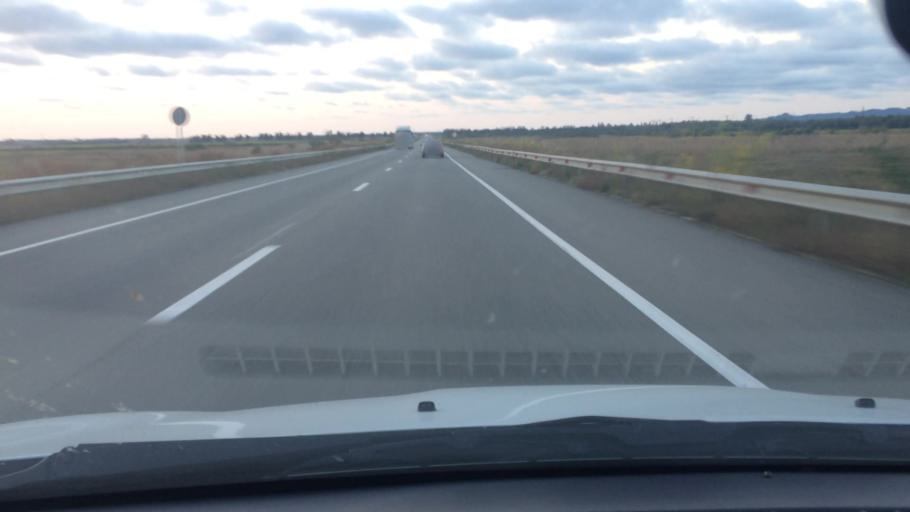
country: GE
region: Ajaria
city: Ochkhamuri
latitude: 41.8724
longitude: 41.8292
